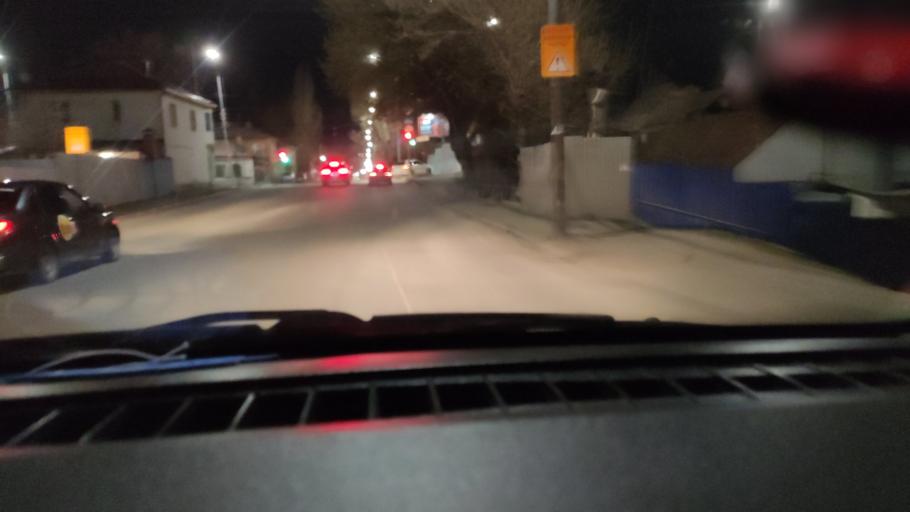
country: RU
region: Saratov
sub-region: Saratovskiy Rayon
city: Saratov
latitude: 51.5424
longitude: 46.0403
